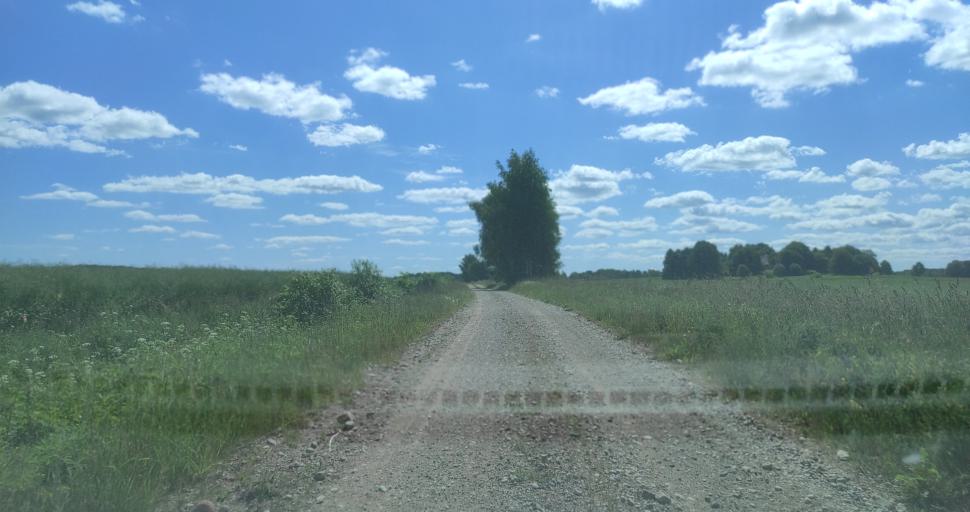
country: LV
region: Aizpute
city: Aizpute
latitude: 56.8624
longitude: 21.7023
